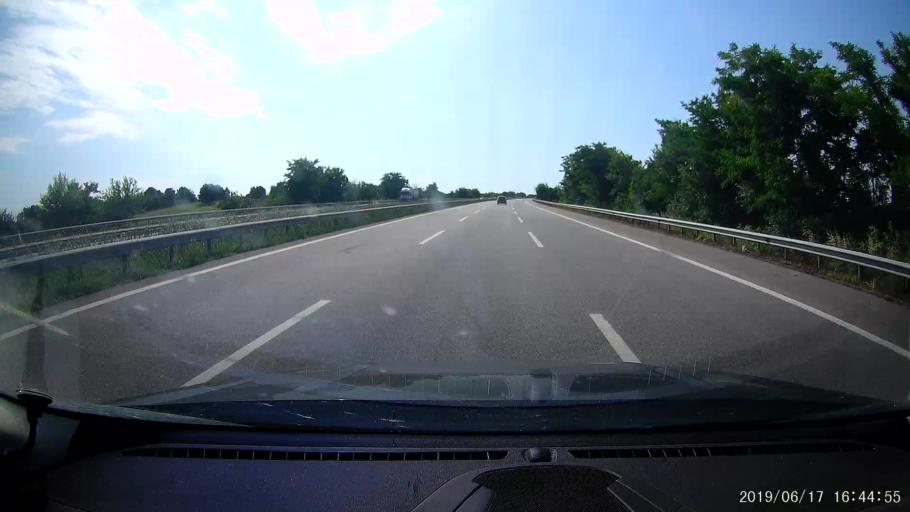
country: TR
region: Kirklareli
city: Luleburgaz
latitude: 41.4831
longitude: 27.2467
